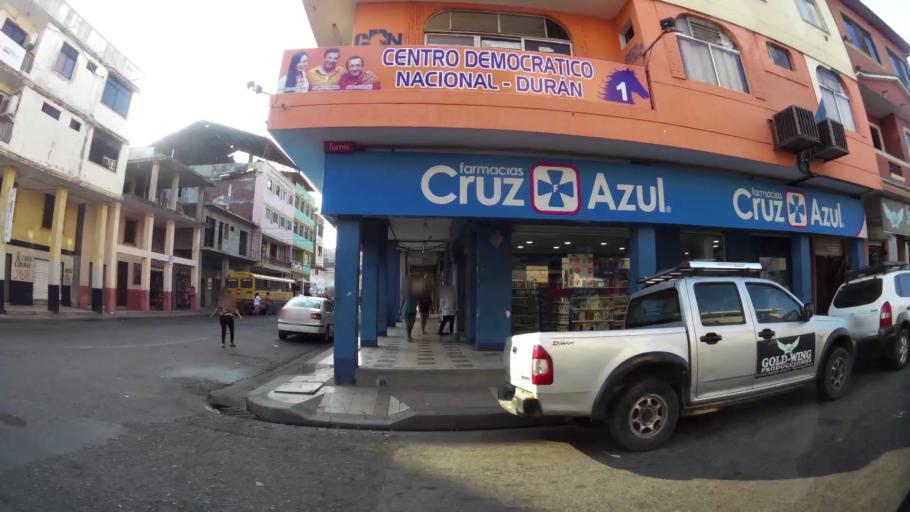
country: EC
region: Guayas
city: Eloy Alfaro
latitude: -2.1709
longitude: -79.8534
